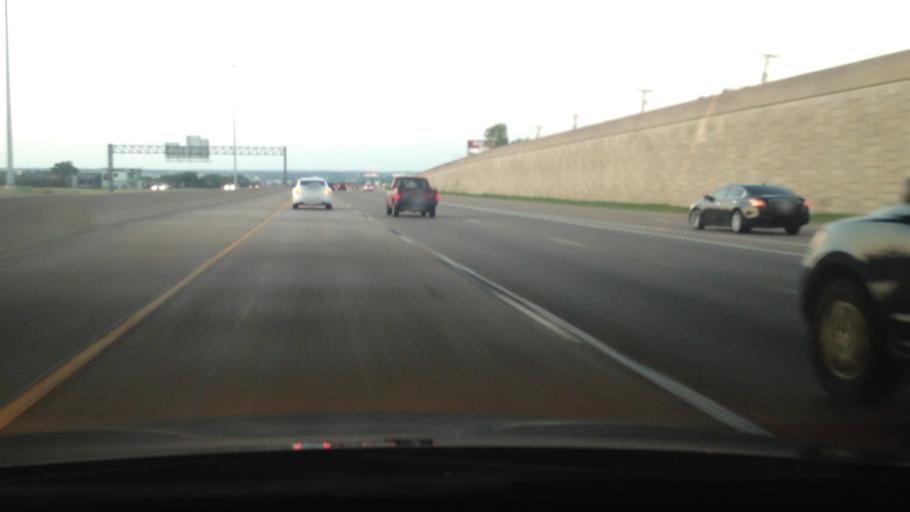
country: US
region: Texas
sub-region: Tarrant County
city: Richland Hills
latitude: 32.7663
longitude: -97.2127
